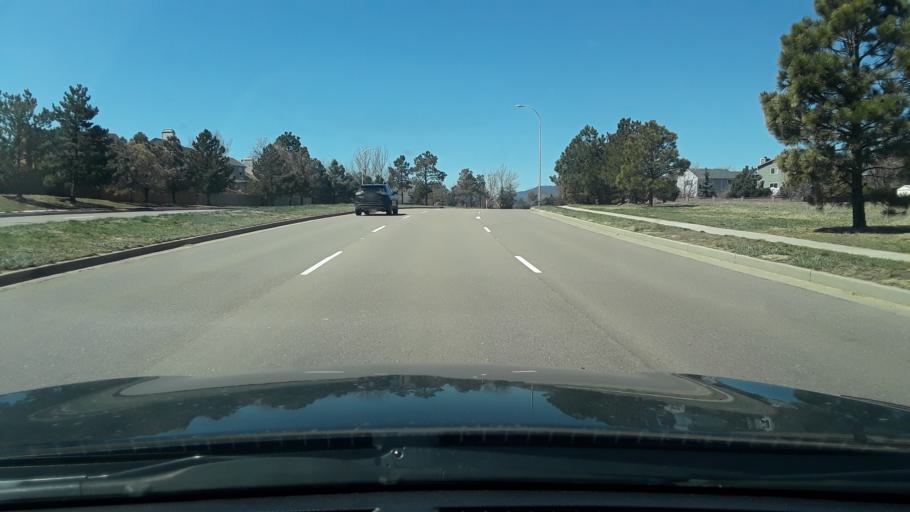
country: US
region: Colorado
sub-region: El Paso County
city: Black Forest
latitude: 38.9547
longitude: -104.7429
